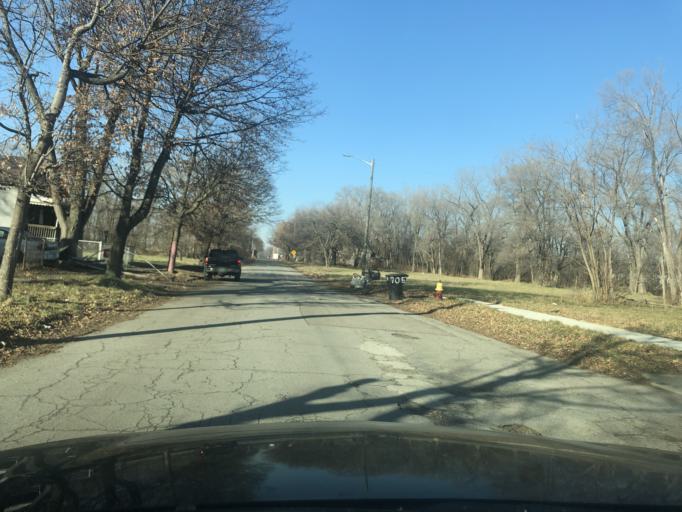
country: US
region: Michigan
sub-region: Wayne County
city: Detroit
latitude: 42.3058
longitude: -83.0918
